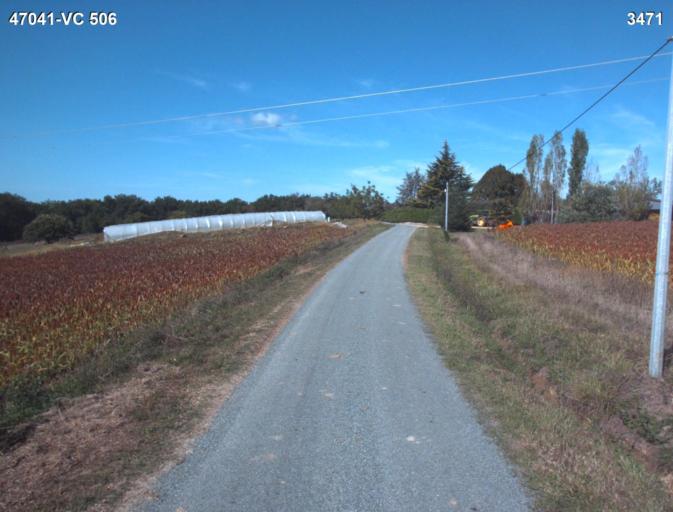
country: FR
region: Aquitaine
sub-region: Departement du Lot-et-Garonne
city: Port-Sainte-Marie
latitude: 44.1885
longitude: 0.3846
